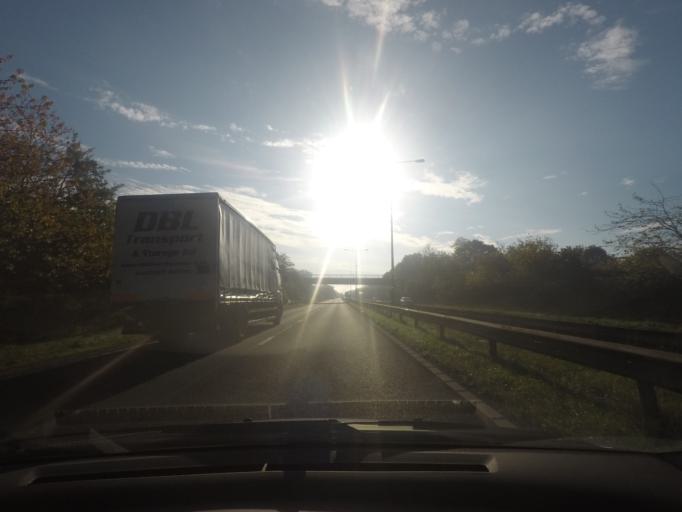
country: GB
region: England
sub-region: East Riding of Yorkshire
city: Brantingham
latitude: 53.7514
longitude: -0.5788
